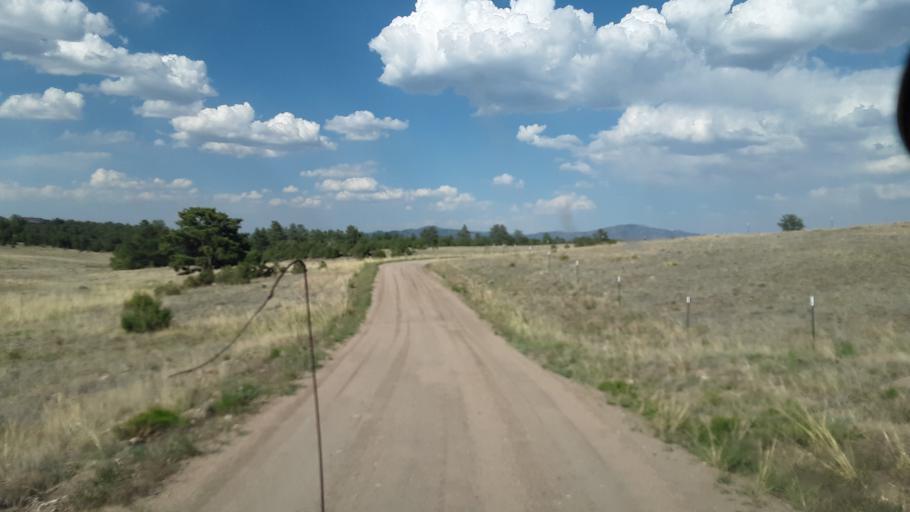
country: US
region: Colorado
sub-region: Custer County
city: Westcliffe
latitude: 38.2716
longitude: -105.4732
